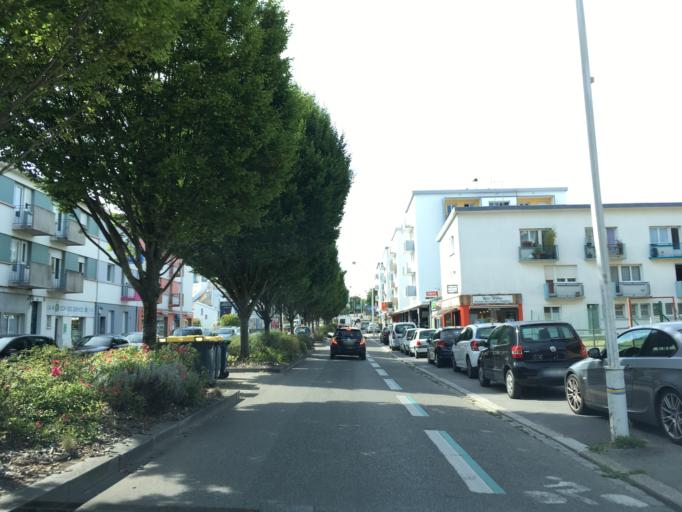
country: FR
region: Brittany
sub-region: Departement du Morbihan
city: Lorient
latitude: 47.7507
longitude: -3.3676
